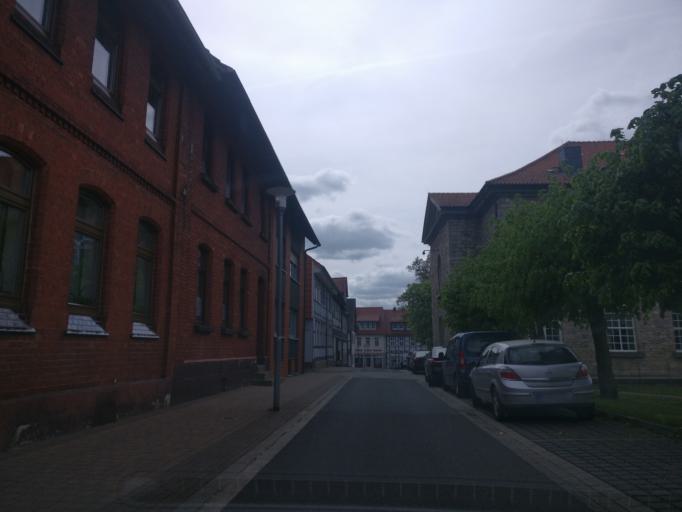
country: DE
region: Lower Saxony
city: Dransfeld
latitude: 51.5038
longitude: 9.7600
